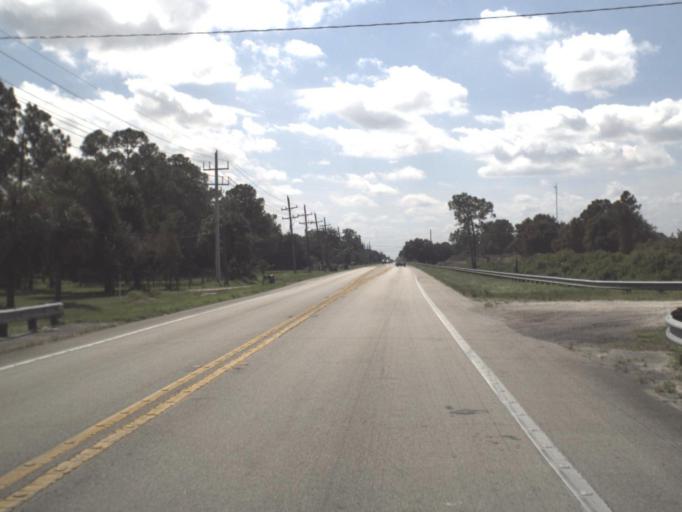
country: US
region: Florida
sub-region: Hendry County
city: LaBelle
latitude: 26.7105
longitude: -81.4374
